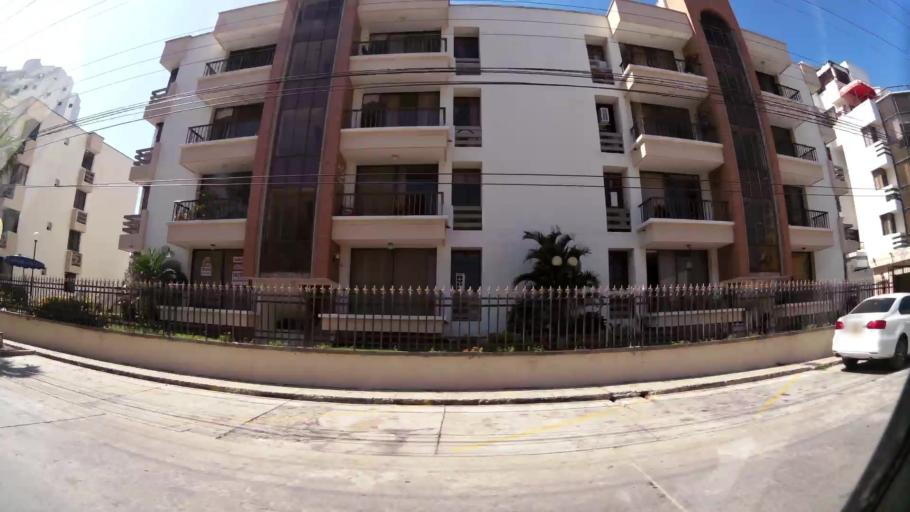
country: CO
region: Atlantico
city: Barranquilla
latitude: 11.0169
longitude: -74.8186
